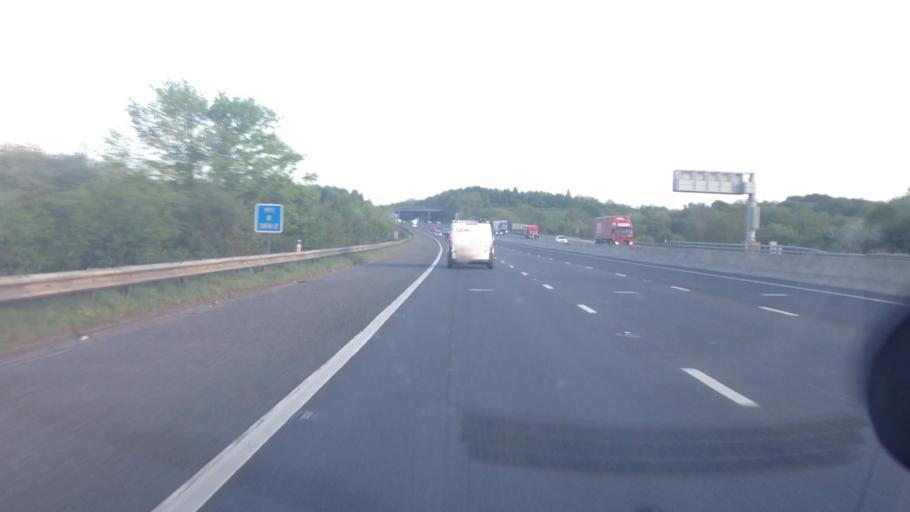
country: GB
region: England
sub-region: Sheffield
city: Chapletown
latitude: 53.4843
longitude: -1.4667
